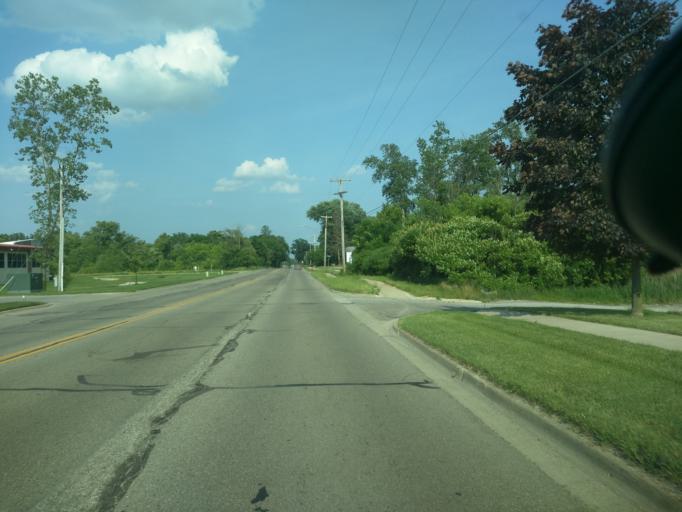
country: US
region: Michigan
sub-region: Jackson County
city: Jackson
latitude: 42.2765
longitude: -84.4509
